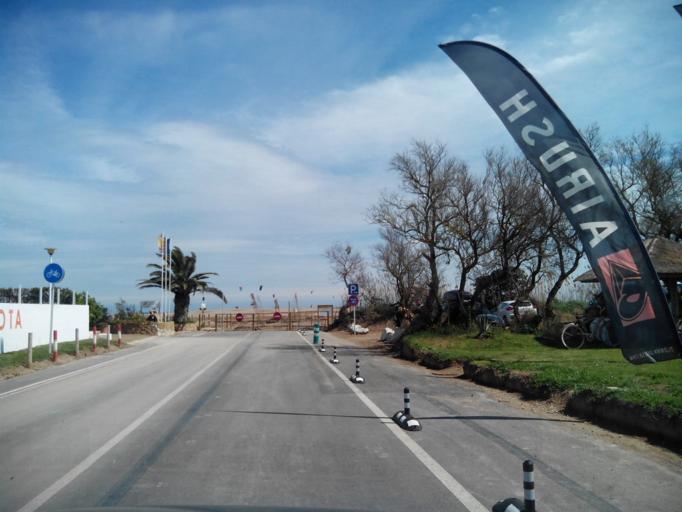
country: ES
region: Catalonia
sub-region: Provincia de Girona
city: Sant Pere Pescador
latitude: 42.1887
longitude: 3.1080
